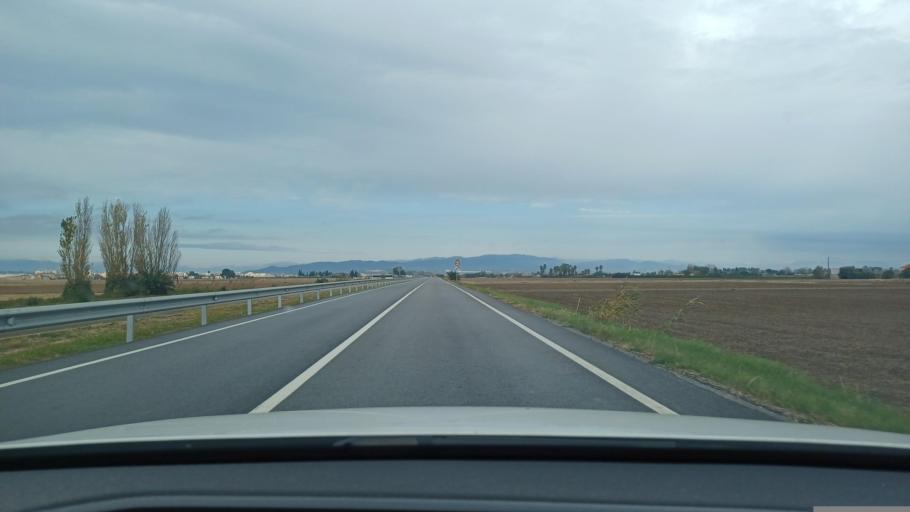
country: ES
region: Catalonia
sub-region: Provincia de Tarragona
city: Amposta
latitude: 40.6835
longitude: 0.5905
